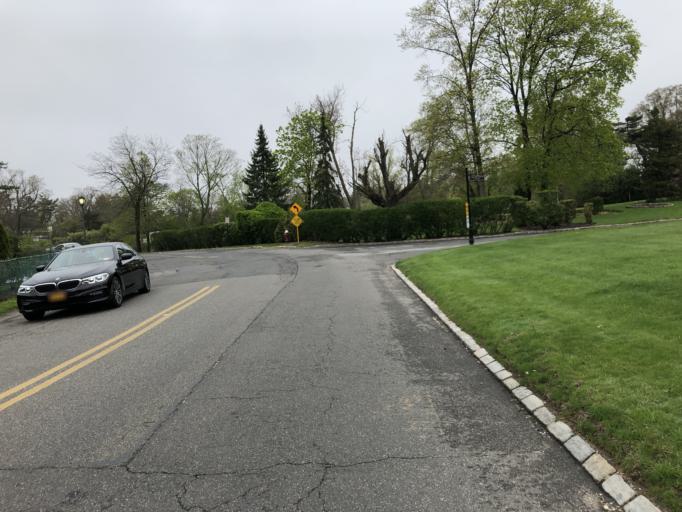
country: US
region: New York
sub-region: Nassau County
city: Hewlett
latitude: 40.6375
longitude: -73.6907
